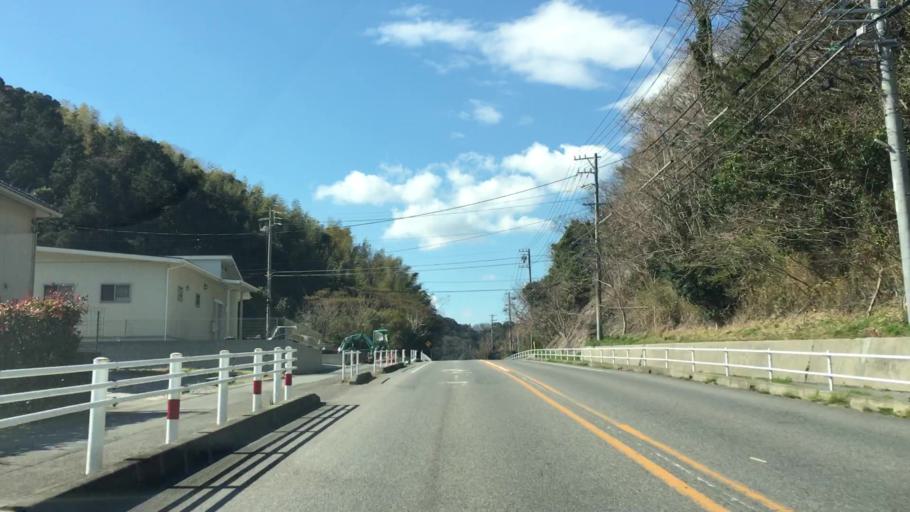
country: JP
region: Aichi
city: Nishio
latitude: 34.7955
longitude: 137.1305
